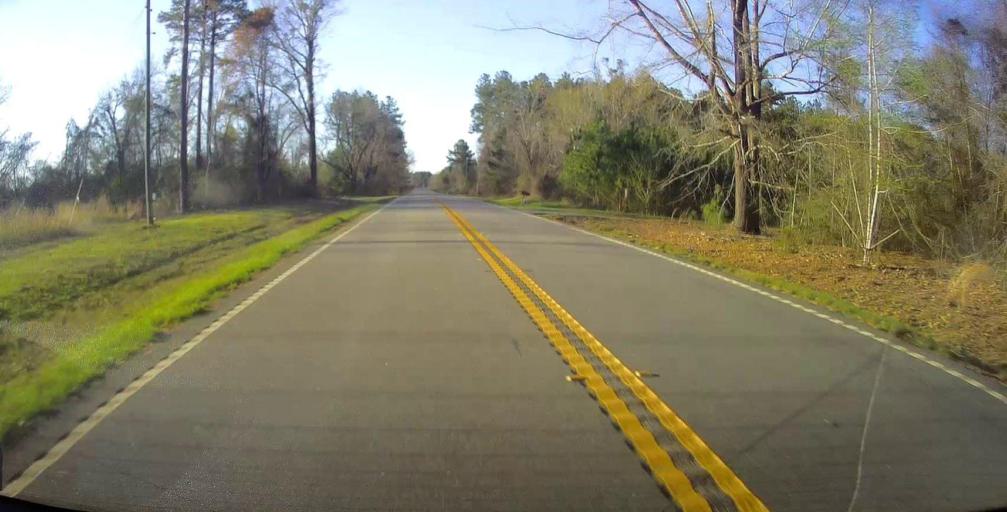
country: US
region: Georgia
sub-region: Wilcox County
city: Abbeville
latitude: 32.1292
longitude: -83.3345
